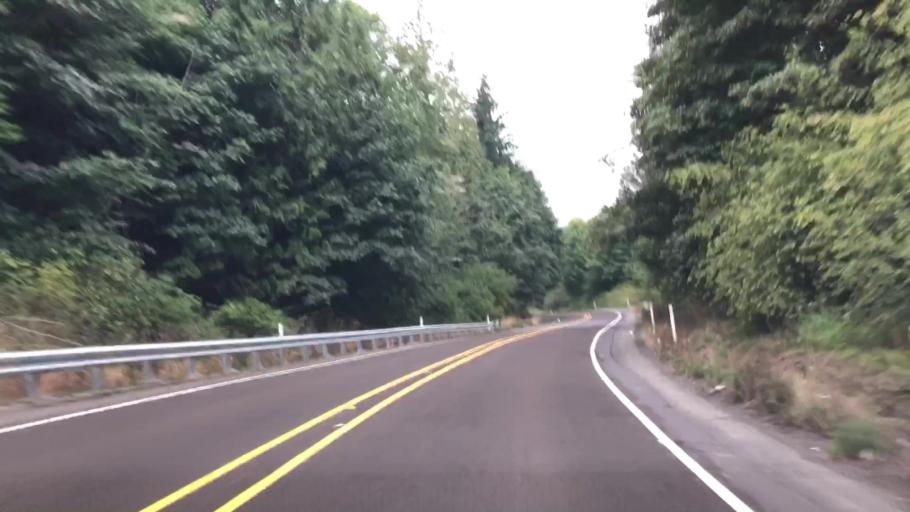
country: US
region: Washington
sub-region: Kitsap County
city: Navy Yard City
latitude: 47.5269
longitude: -122.7288
